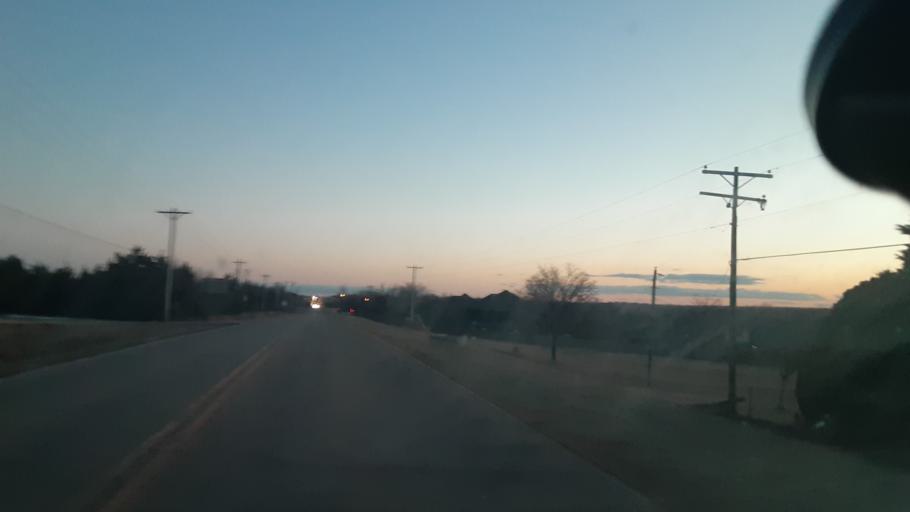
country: US
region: Oklahoma
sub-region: Oklahoma County
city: Edmond
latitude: 35.6620
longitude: -97.4250
